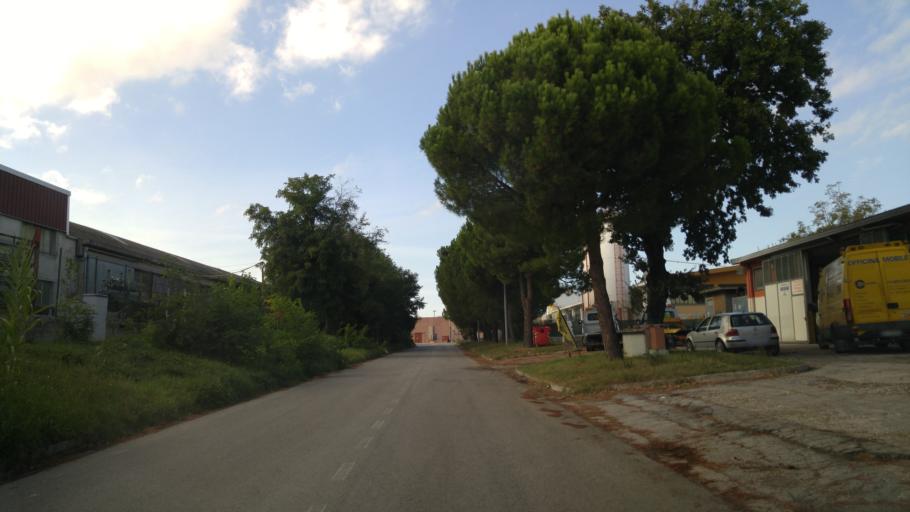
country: IT
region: The Marches
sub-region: Provincia di Pesaro e Urbino
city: Bellocchi
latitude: 43.7982
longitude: 13.0128
